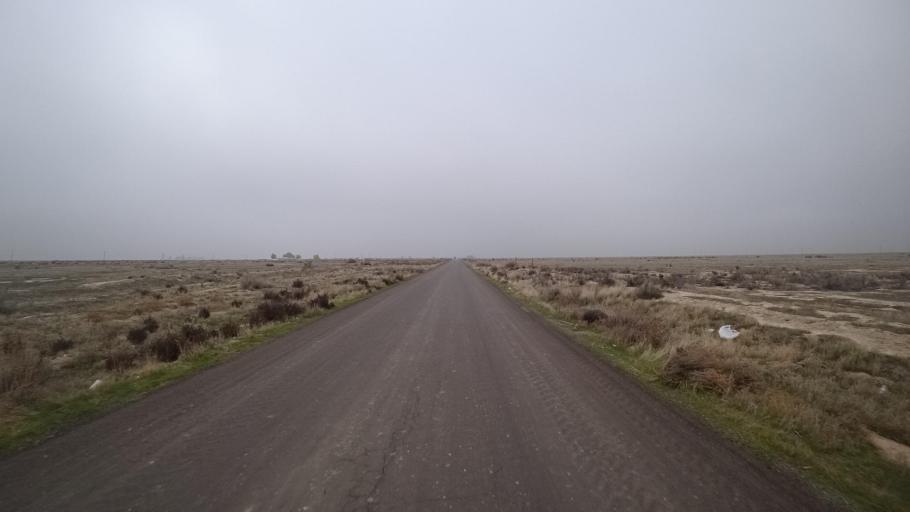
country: US
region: California
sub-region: Tulare County
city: Alpaugh
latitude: 35.7184
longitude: -119.4726
